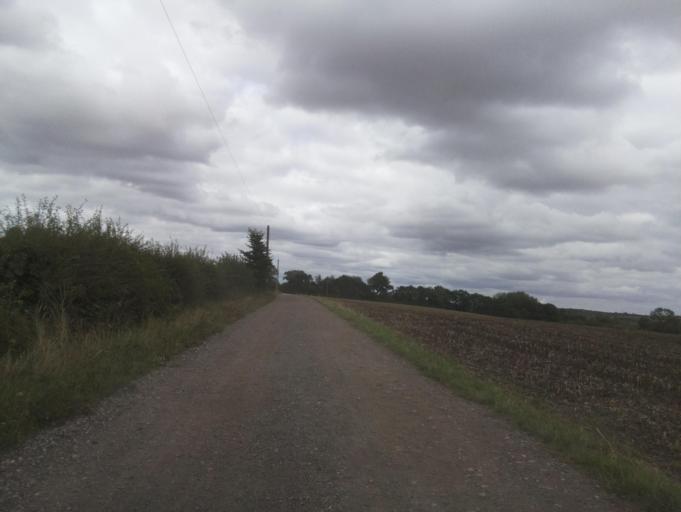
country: GB
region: England
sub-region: Nottinghamshire
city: East Leake
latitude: 52.8431
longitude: -1.1934
